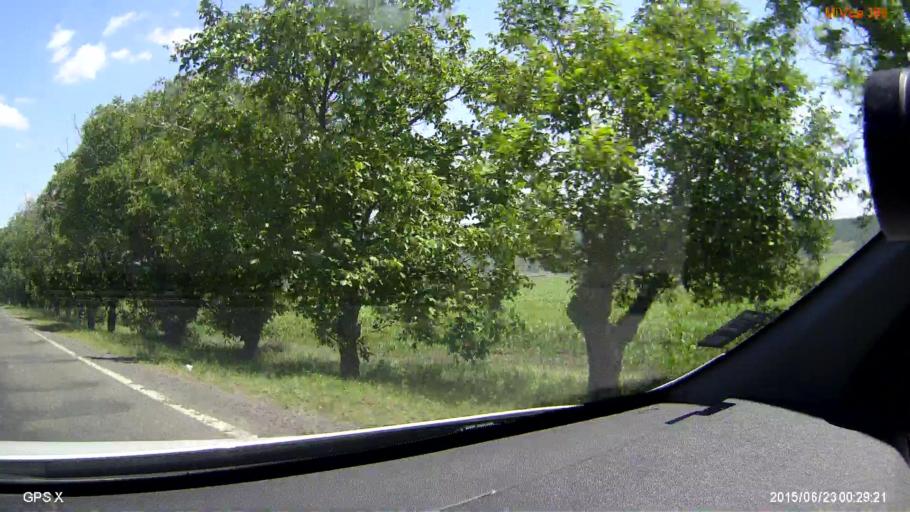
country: RO
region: Iasi
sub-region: Comuna Grozesti
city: Grozesti
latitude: 47.0369
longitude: 28.0841
